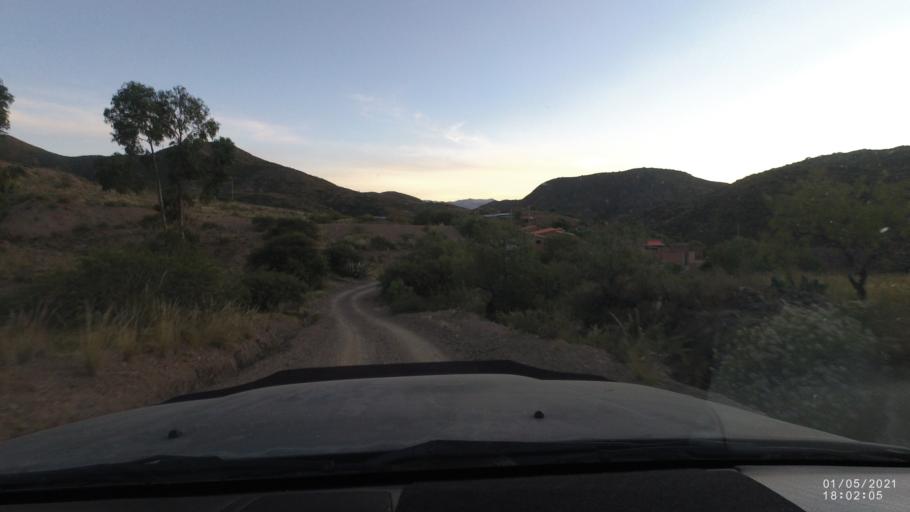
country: BO
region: Cochabamba
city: Capinota
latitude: -17.6868
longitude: -66.1730
